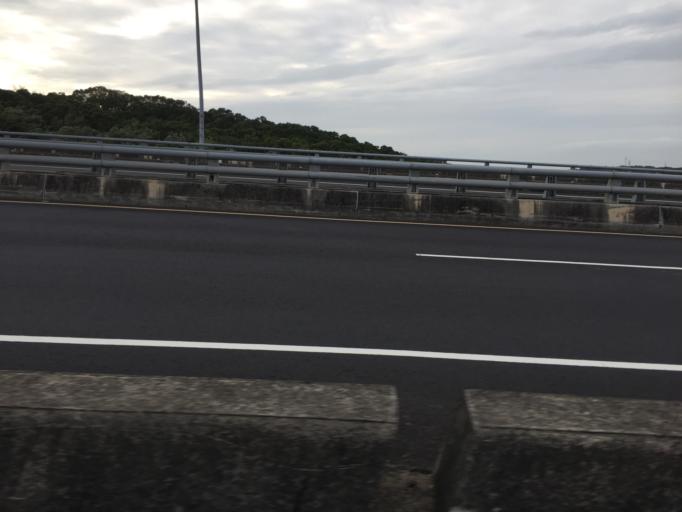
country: TW
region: Taiwan
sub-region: Hsinchu
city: Hsinchu
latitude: 24.7711
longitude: 120.9523
